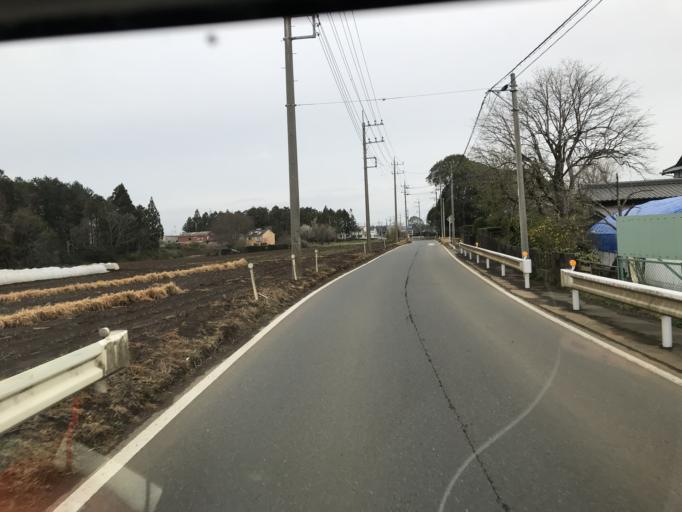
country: JP
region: Chiba
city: Sawara
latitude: 35.8480
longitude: 140.5146
